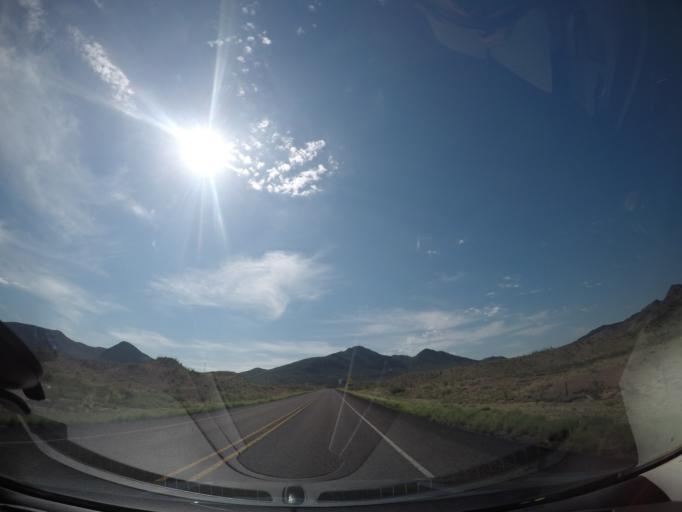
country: US
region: Texas
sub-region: Presidio County
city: Presidio
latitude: 29.4704
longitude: -103.5255
